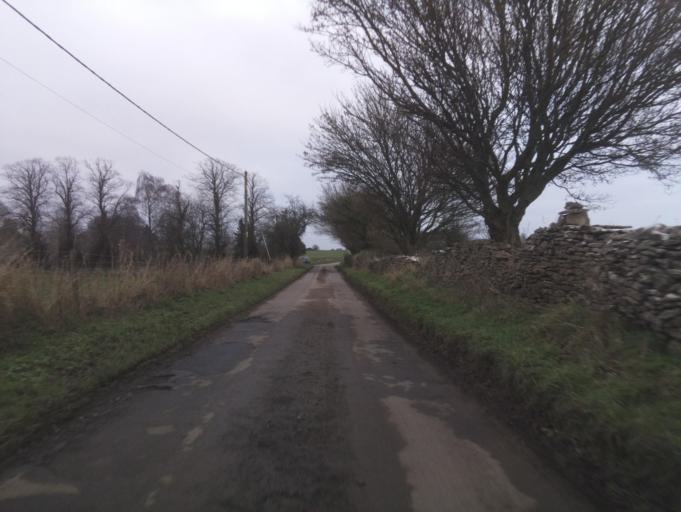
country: GB
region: England
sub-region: Wiltshire
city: Nettleton
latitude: 51.4785
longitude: -2.2822
